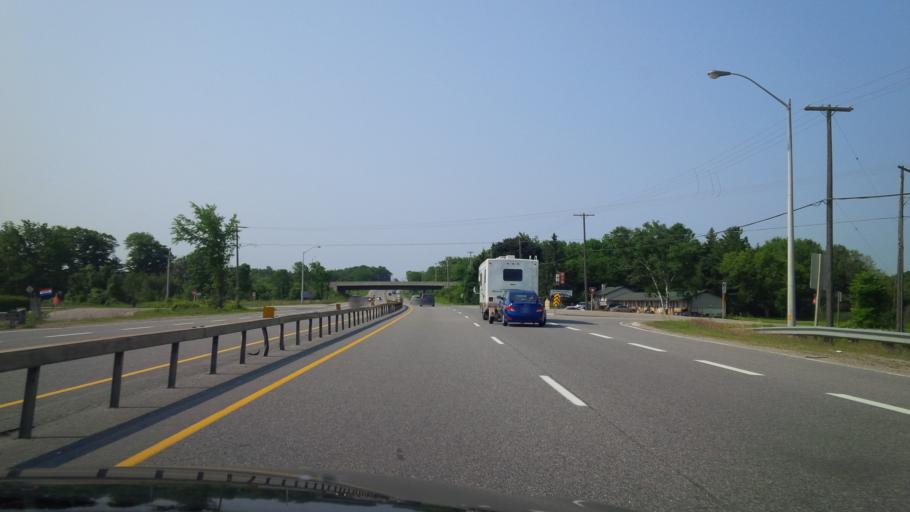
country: CA
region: Ontario
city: Orillia
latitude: 44.6719
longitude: -79.4104
